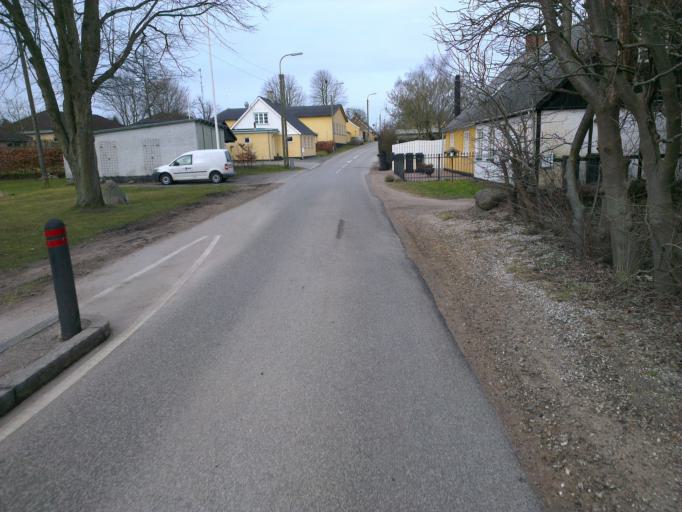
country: DK
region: Capital Region
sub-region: Frederikssund Kommune
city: Skibby
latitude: 55.7941
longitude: 11.9573
